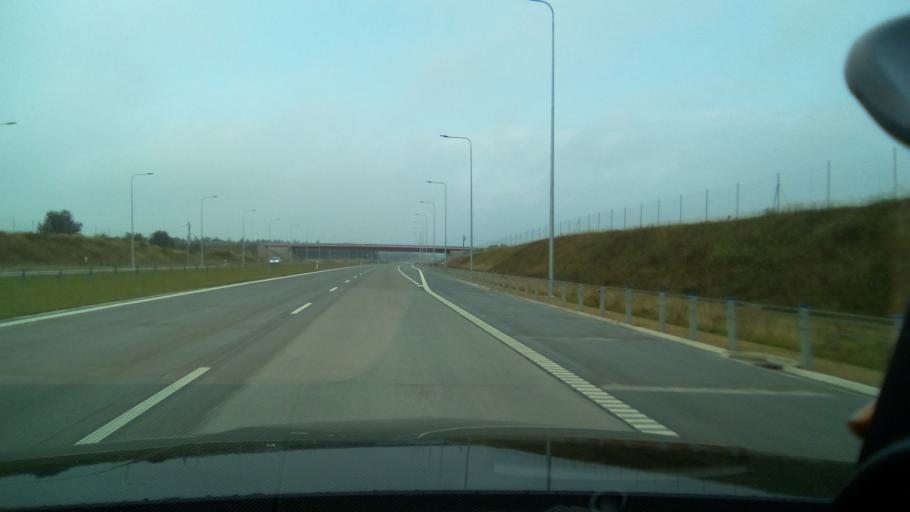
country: PL
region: Silesian Voivodeship
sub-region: Powiat klobucki
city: Kalej
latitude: 50.8166
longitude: 19.0212
